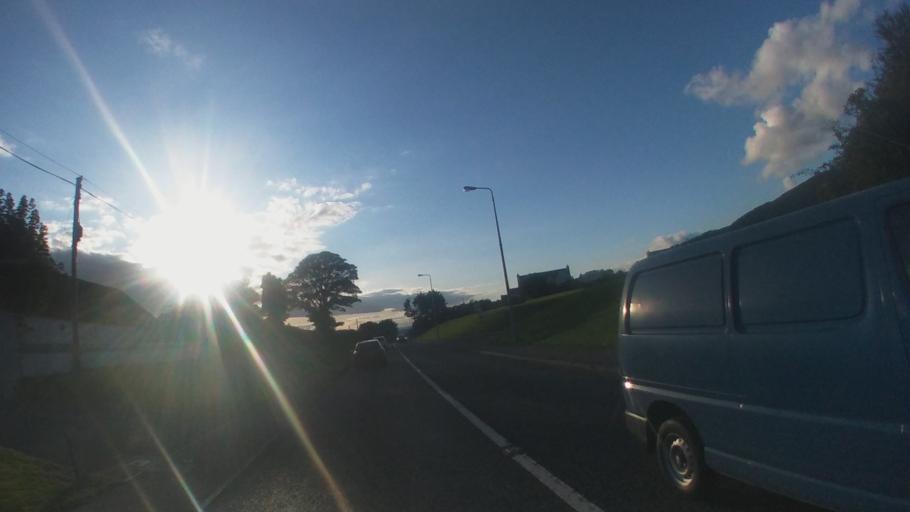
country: IE
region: Leinster
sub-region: Lu
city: Carlingford
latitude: 54.0001
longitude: -6.2667
